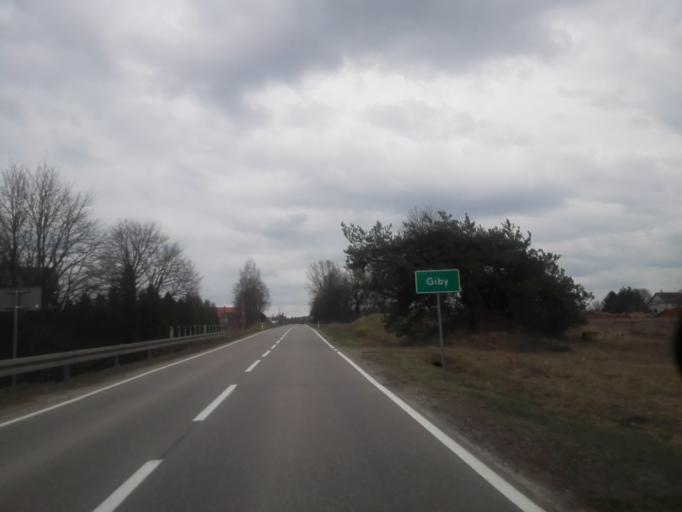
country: PL
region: Podlasie
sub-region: Powiat sejnenski
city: Sejny
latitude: 54.0452
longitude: 23.3557
